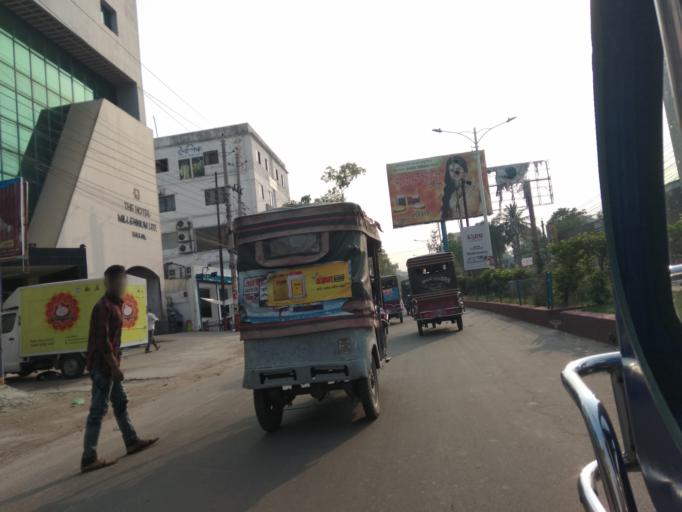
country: BD
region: Khulna
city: Khulna
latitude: 22.8210
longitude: 89.5508
